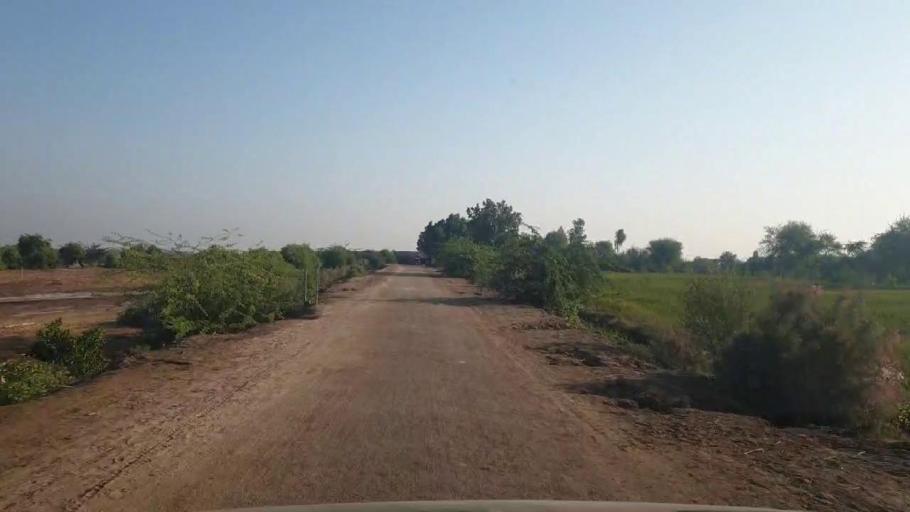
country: PK
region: Sindh
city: Badin
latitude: 24.7168
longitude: 68.8591
